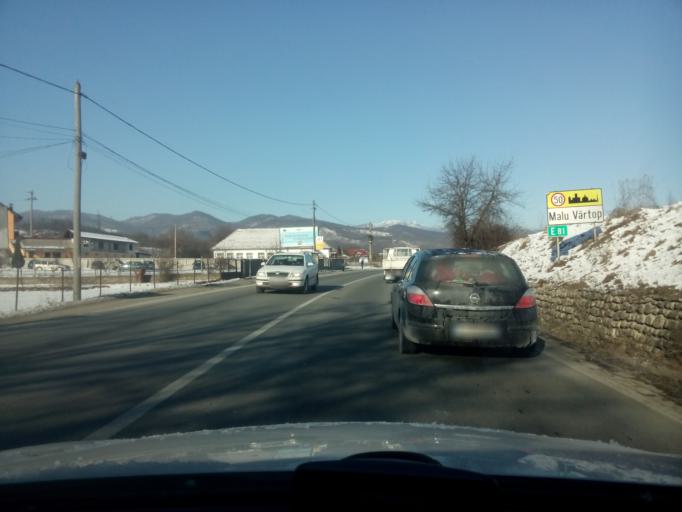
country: RO
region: Valcea
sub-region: Comuna Muereasca
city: Muereasca
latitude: 45.1685
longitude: 24.3667
